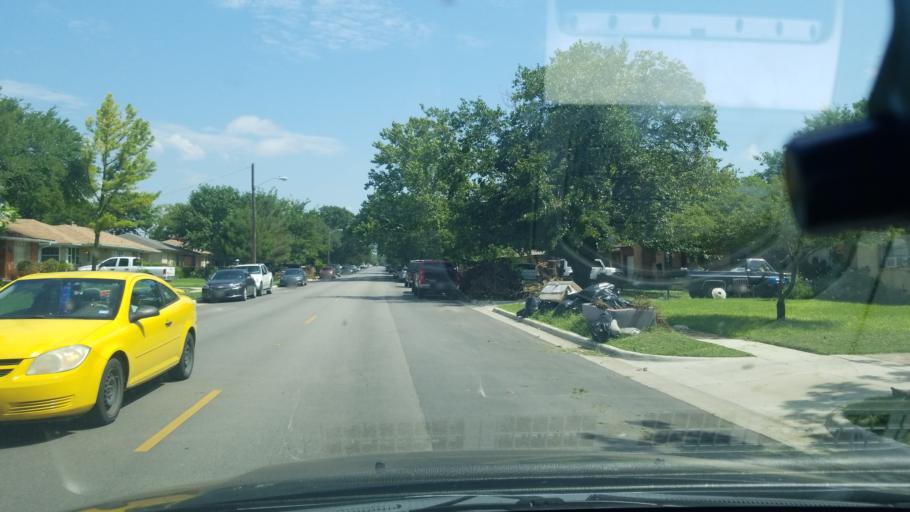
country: US
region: Texas
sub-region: Dallas County
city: Balch Springs
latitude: 32.7496
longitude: -96.6917
